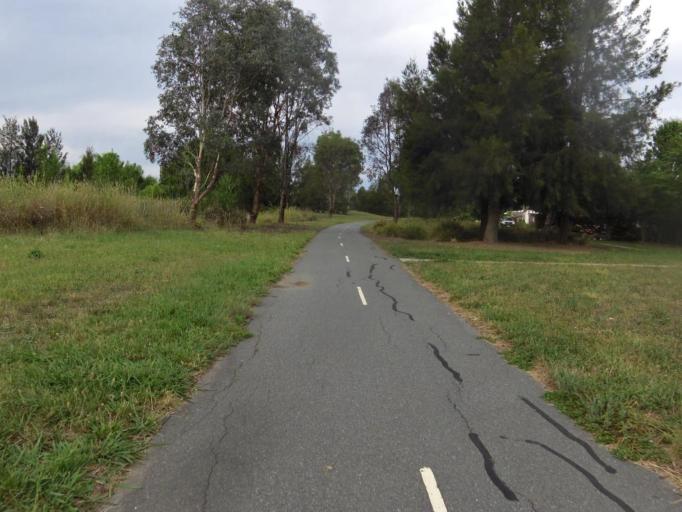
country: AU
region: Australian Capital Territory
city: Kaleen
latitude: -35.1686
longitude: 149.1403
